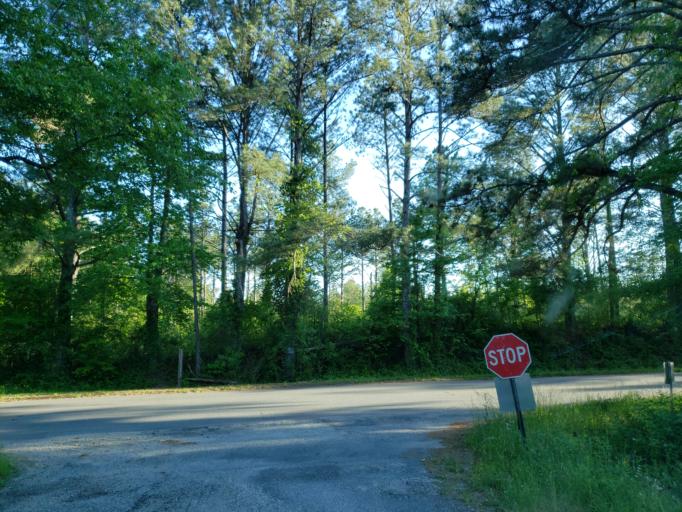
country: US
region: Georgia
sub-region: Haralson County
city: Tallapoosa
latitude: 33.7664
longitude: -85.3283
